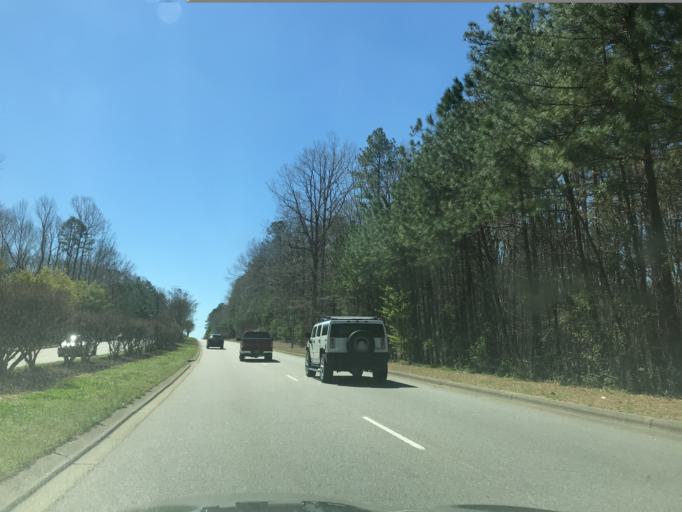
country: US
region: North Carolina
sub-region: Wake County
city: Garner
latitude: 35.7081
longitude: -78.6415
